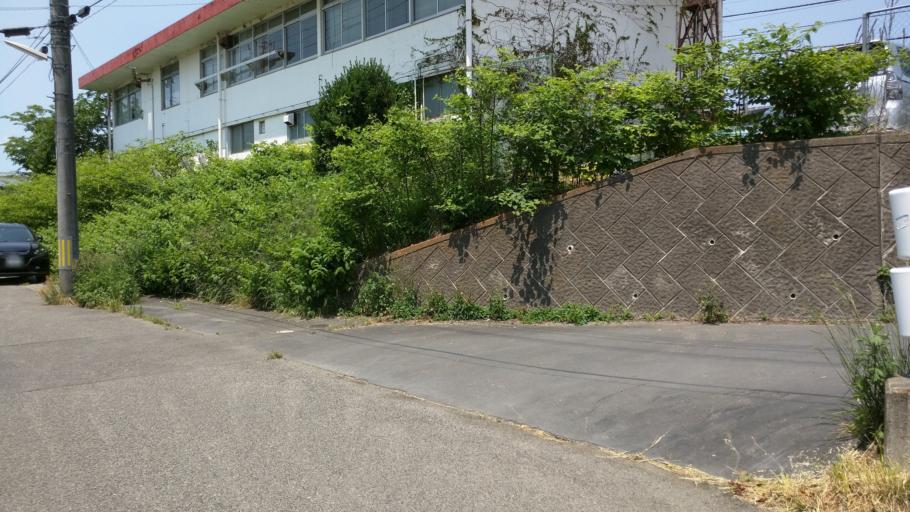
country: JP
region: Fukushima
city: Sukagawa
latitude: 37.1293
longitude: 140.2155
